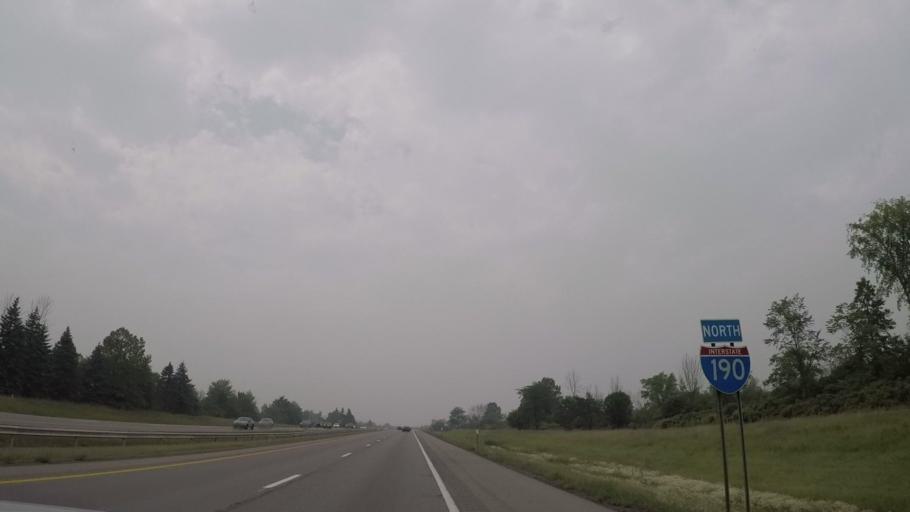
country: US
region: New York
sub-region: Erie County
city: Grandyle Village
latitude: 43.0290
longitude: -78.9793
